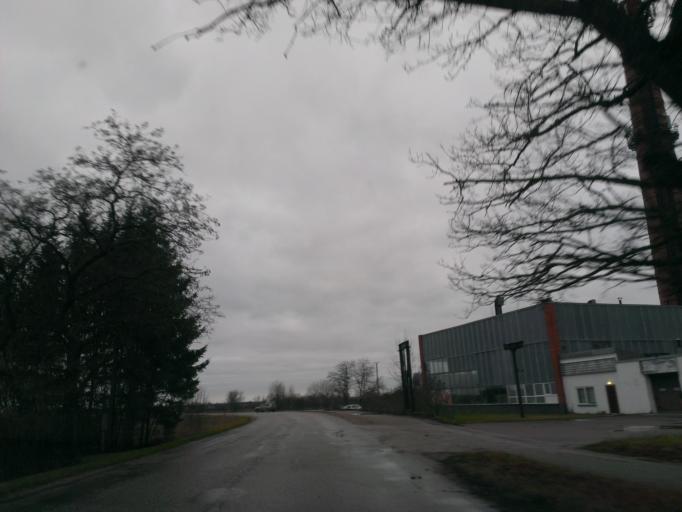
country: LV
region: Adazi
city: Adazi
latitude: 57.0687
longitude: 24.3550
